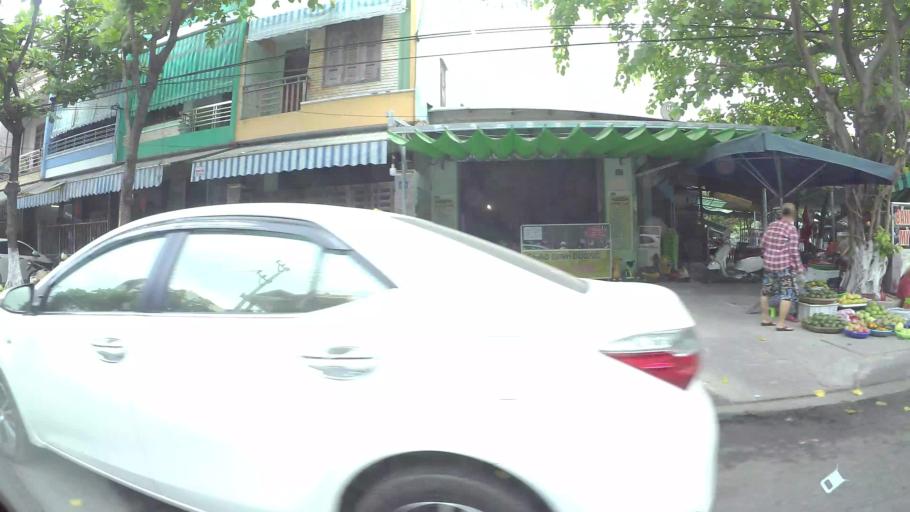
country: VN
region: Da Nang
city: Thanh Khe
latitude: 16.0704
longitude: 108.1874
